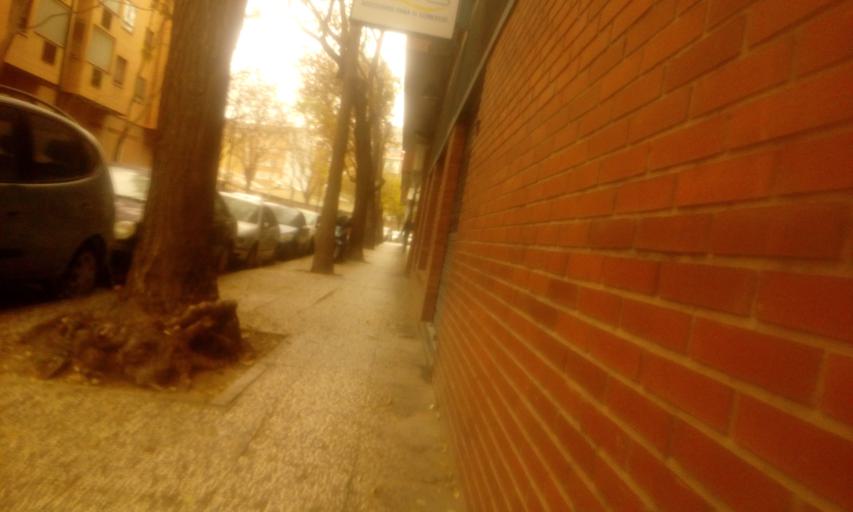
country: ES
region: Aragon
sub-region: Provincia de Zaragoza
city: Zaragoza
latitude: 41.6533
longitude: -0.8695
